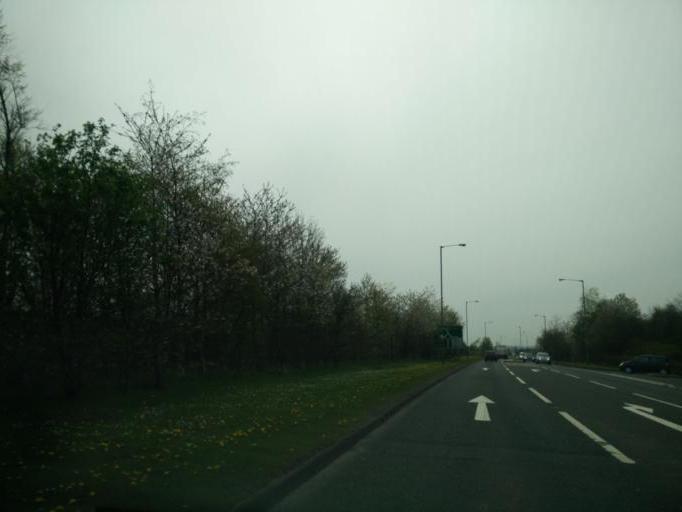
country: GB
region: England
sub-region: County Durham
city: Bishop Auckland
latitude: 54.6405
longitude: -1.6842
